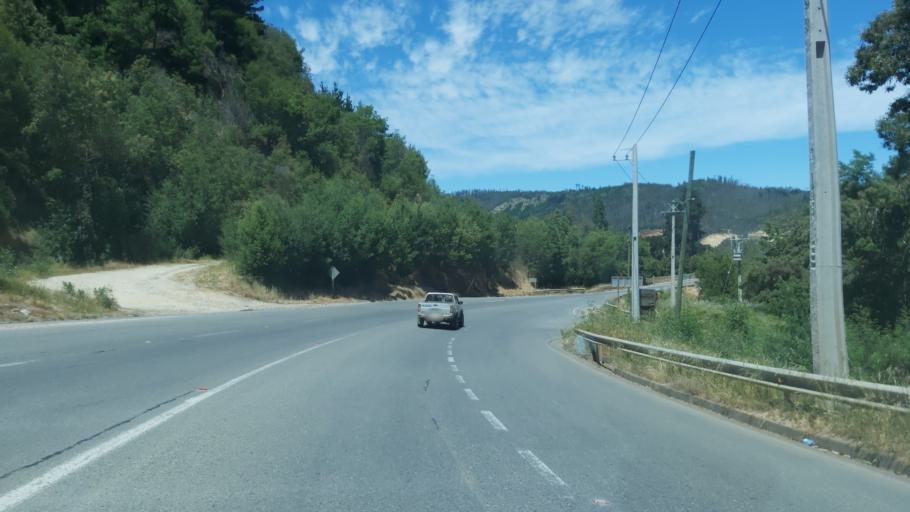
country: CL
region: Maule
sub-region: Provincia de Talca
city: Constitucion
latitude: -35.3353
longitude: -72.3884
